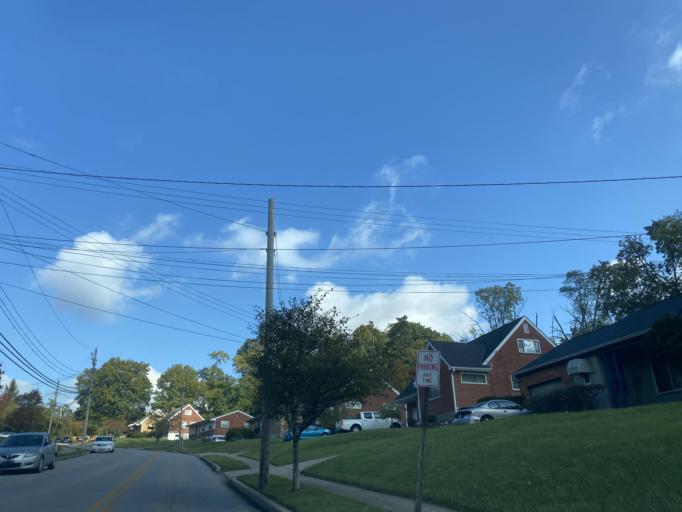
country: US
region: Kentucky
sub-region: Campbell County
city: Fort Thomas
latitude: 39.0912
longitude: -84.4570
